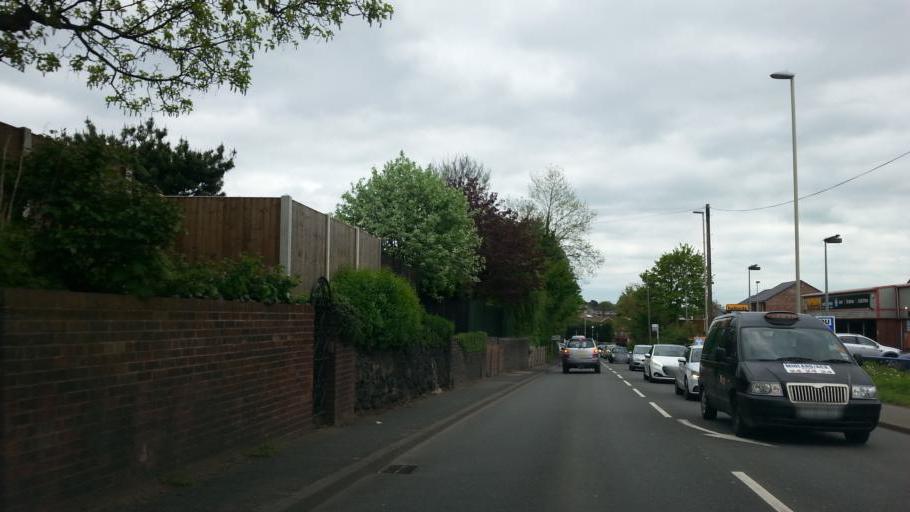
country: GB
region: England
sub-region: Dudley
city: Stourbridge
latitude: 52.4755
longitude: -2.1570
